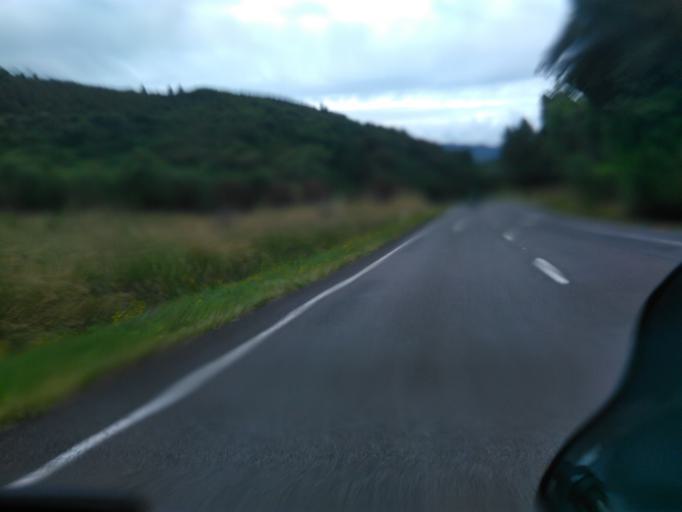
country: NZ
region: Bay of Plenty
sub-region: Opotiki District
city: Opotiki
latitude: -38.2339
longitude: 177.3110
